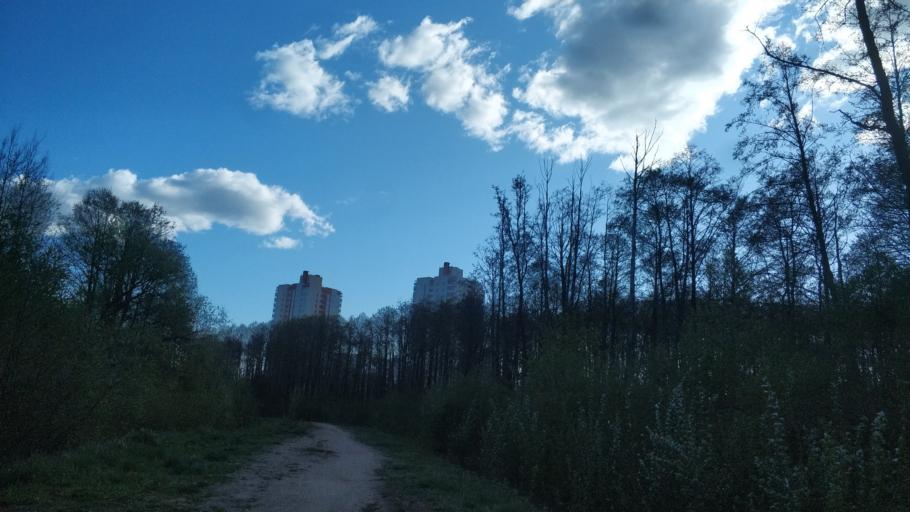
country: BY
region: Minsk
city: Minsk
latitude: 53.8683
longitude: 27.5791
